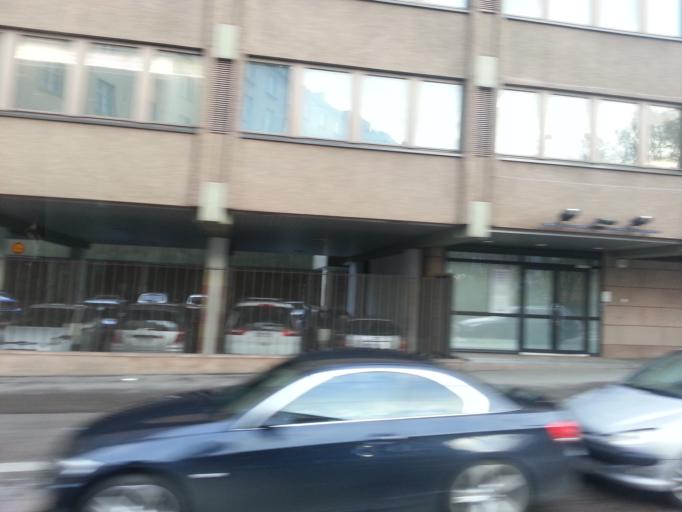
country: FI
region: Uusimaa
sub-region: Helsinki
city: Helsinki
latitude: 60.1858
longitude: 24.9514
